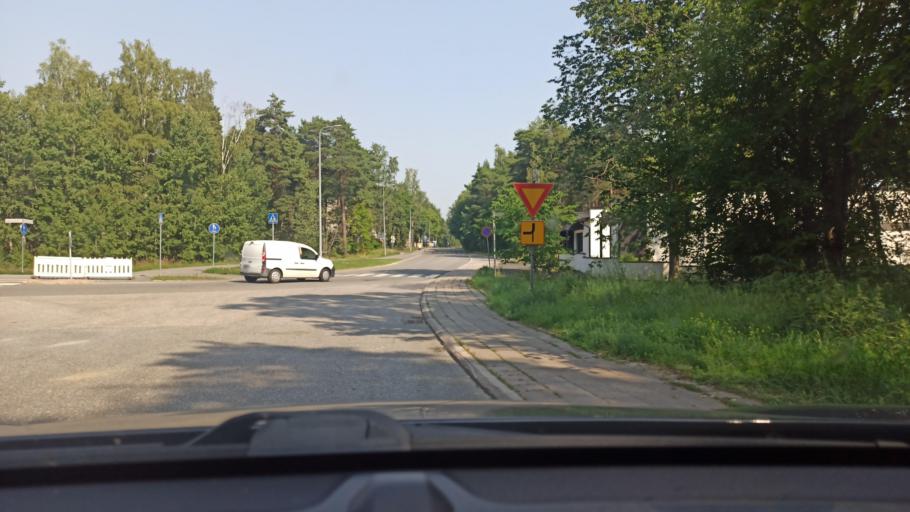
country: FI
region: Varsinais-Suomi
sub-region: Turku
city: Turku
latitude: 60.4611
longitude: 22.2183
